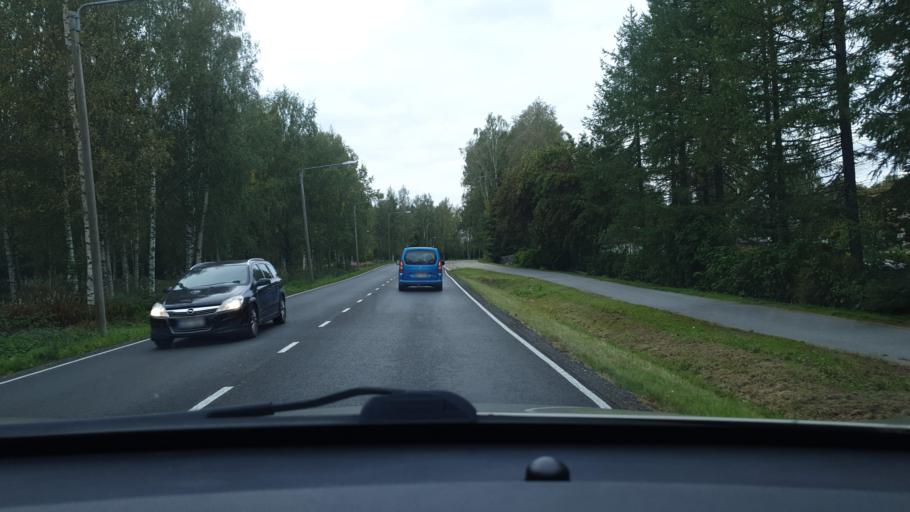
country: FI
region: Ostrobothnia
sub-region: Vaasa
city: Teeriniemi
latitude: 63.0872
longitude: 21.6944
